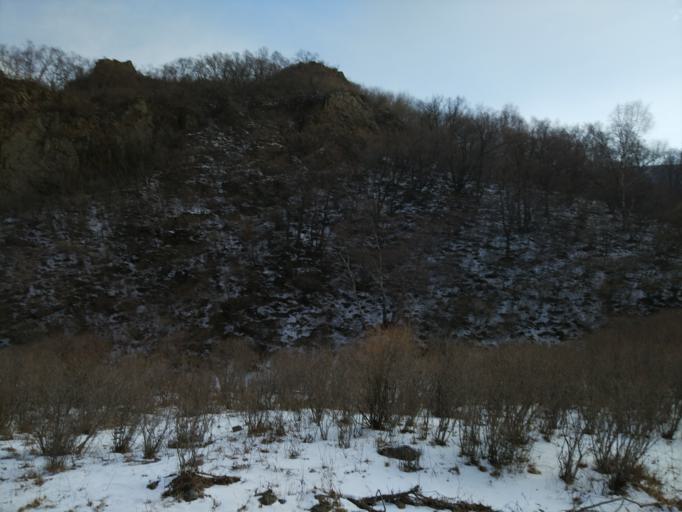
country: CN
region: Hebei
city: Xiwanzi
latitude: 40.8410
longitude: 115.4589
